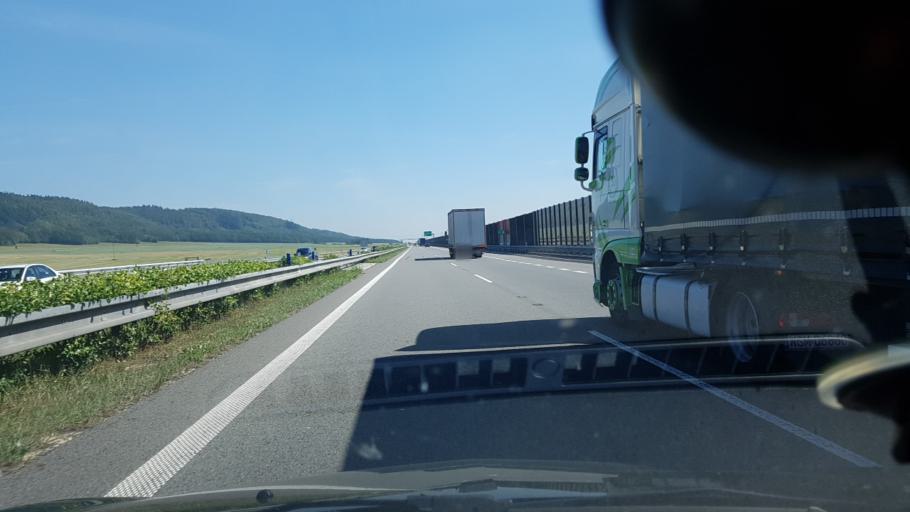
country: CZ
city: Odry
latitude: 49.6414
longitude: 17.8691
